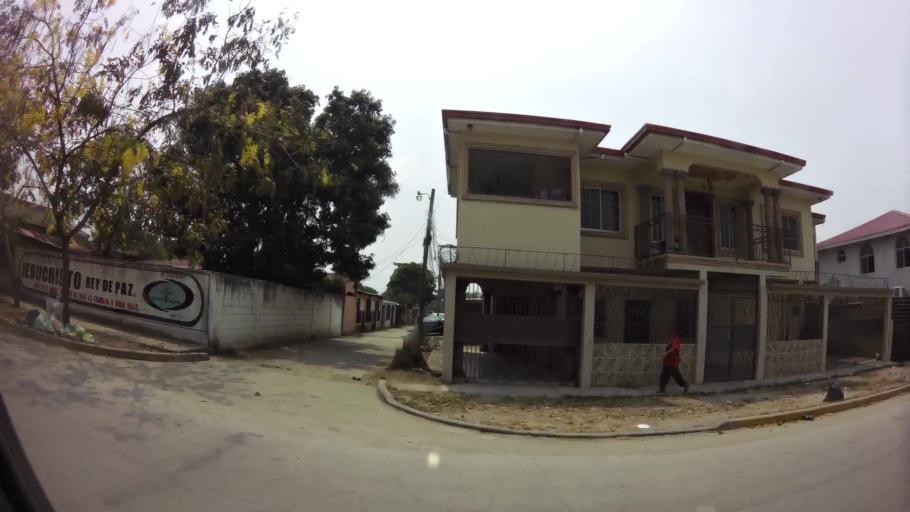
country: HN
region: Cortes
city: San Pedro Sula
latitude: 15.4807
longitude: -88.0215
